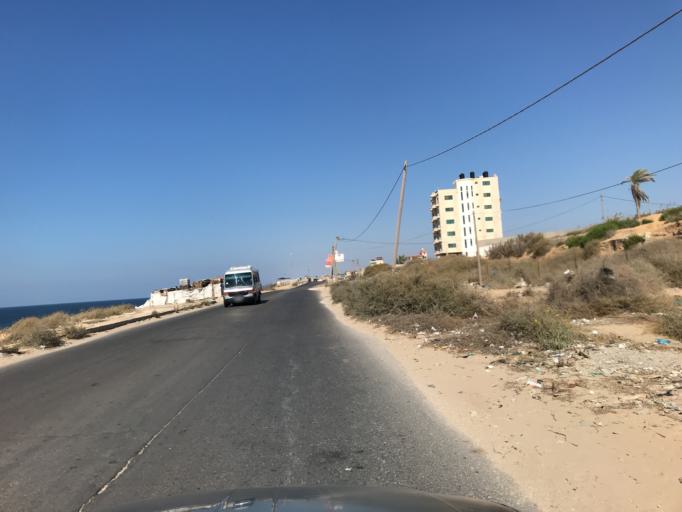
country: PS
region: Gaza Strip
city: Az Zuwaydah
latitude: 31.4462
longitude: 34.3589
